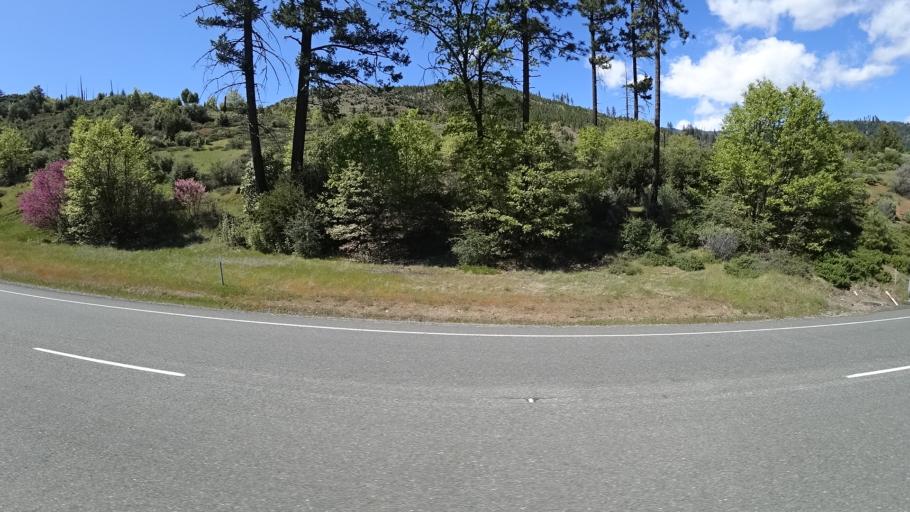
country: US
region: California
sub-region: Trinity County
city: Weaverville
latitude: 40.7419
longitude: -122.9774
